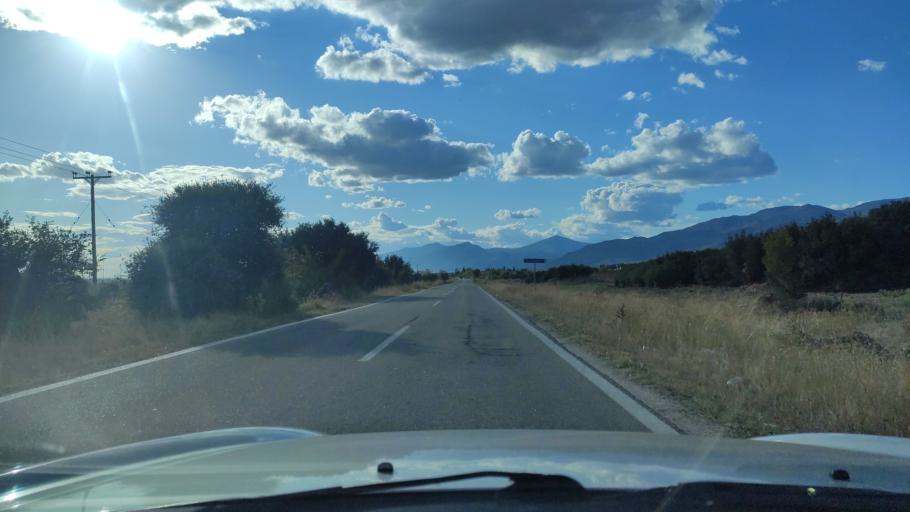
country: GR
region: East Macedonia and Thrace
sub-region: Nomos Xanthis
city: Selero
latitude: 41.1216
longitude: 25.0759
